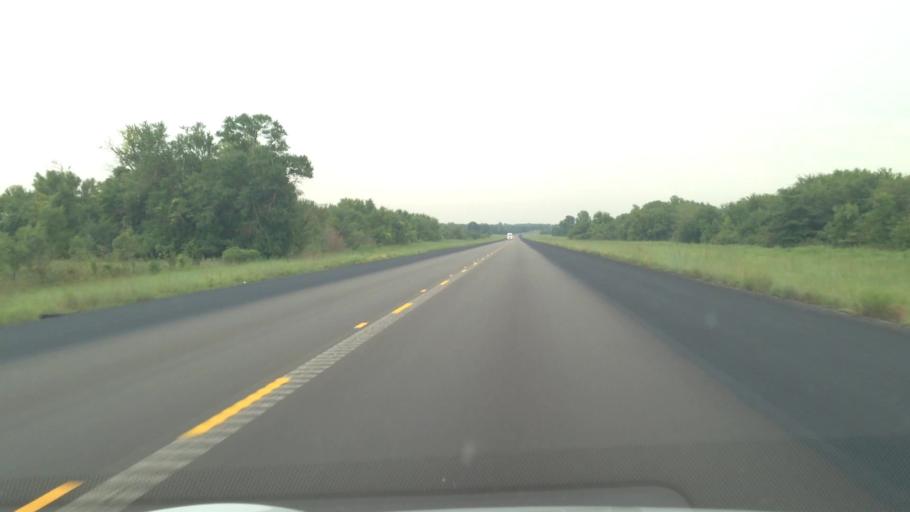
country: US
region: Kansas
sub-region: Cherokee County
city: Baxter Springs
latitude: 37.0391
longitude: -94.7090
